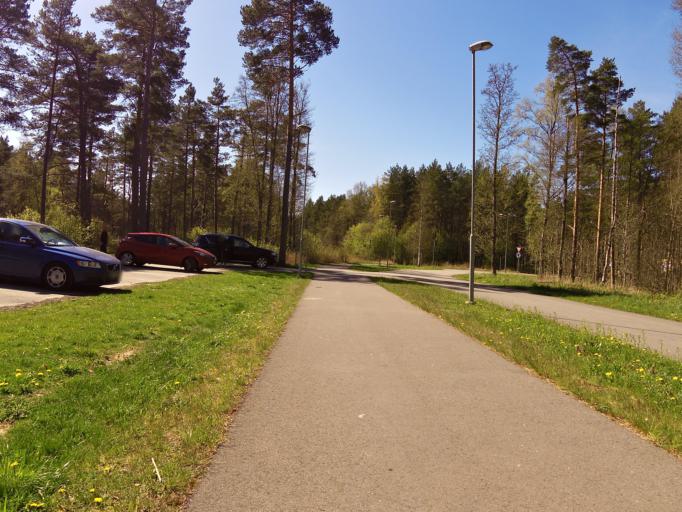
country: EE
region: Harju
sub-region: Raasiku vald
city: Raasiku
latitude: 59.4945
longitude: 25.1787
